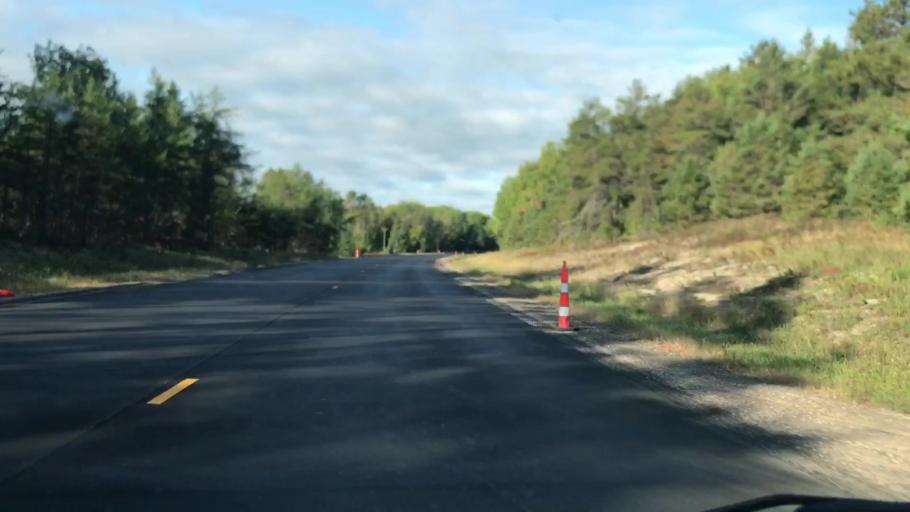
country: US
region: Michigan
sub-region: Mackinac County
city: Saint Ignace
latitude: 46.3470
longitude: -84.9180
